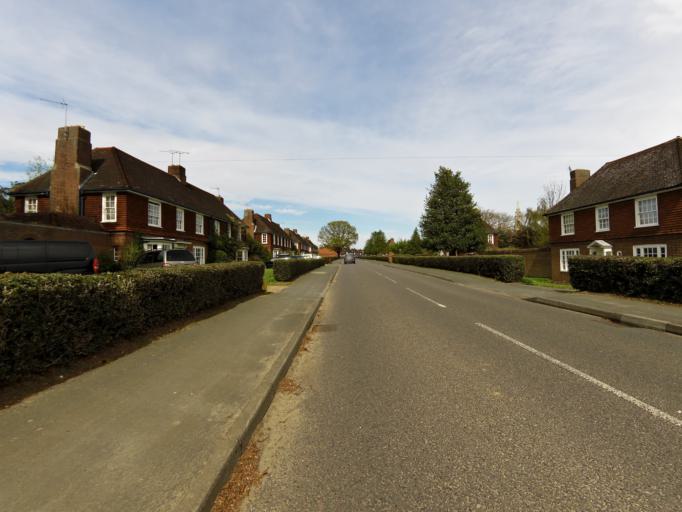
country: GB
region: England
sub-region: Essex
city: Mistley
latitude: 51.9716
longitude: 1.1464
